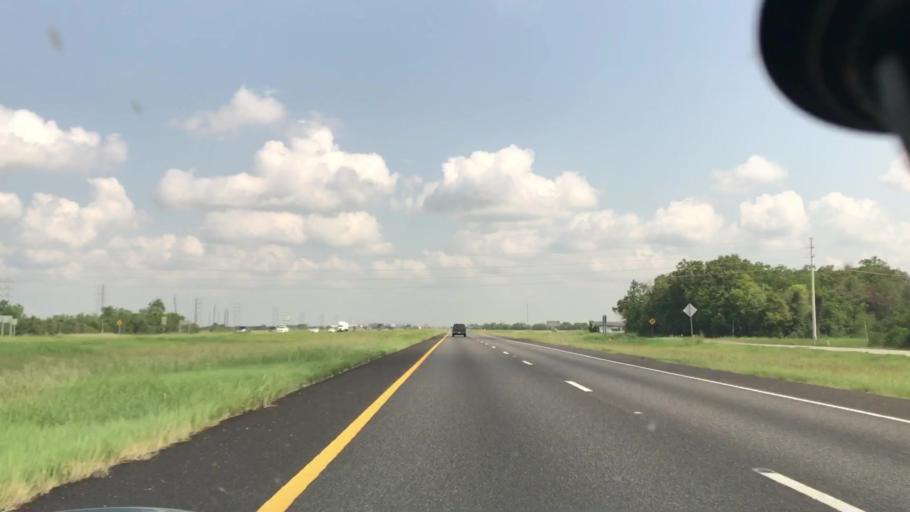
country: US
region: Texas
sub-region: Brazoria County
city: Rosharon
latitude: 29.4041
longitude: -95.4268
